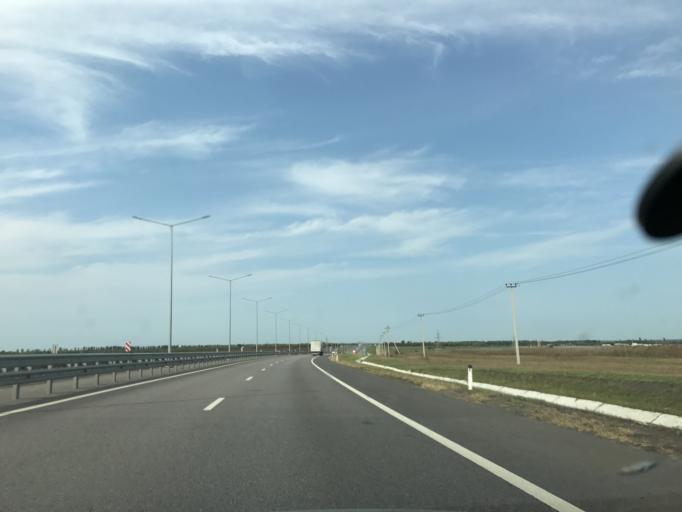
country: RU
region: Voronezj
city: Kashirskoye
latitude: 51.4862
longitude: 39.5355
